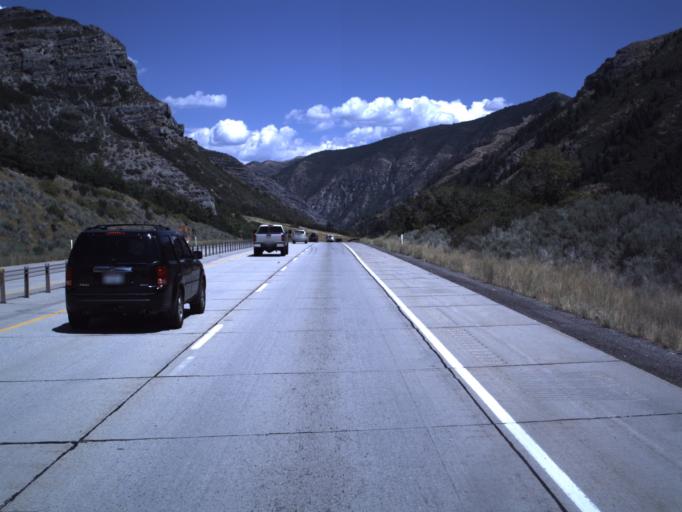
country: US
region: Utah
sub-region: Utah County
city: Orem
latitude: 40.3464
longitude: -111.5975
